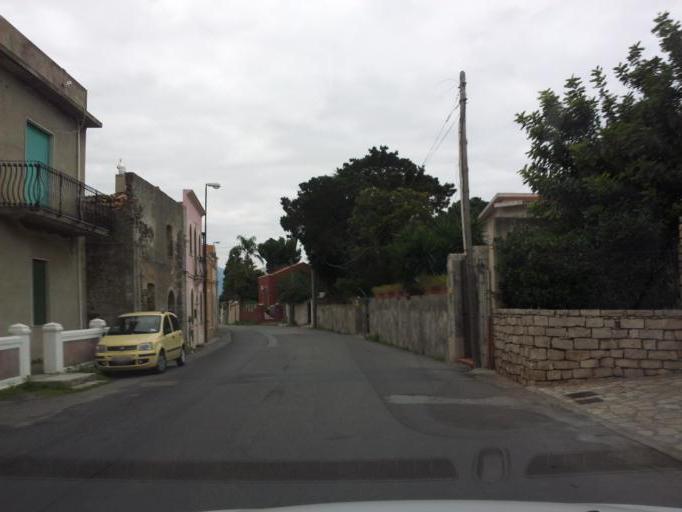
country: IT
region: Sicily
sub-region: Messina
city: Milazzo
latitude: 38.2386
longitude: 15.2454
